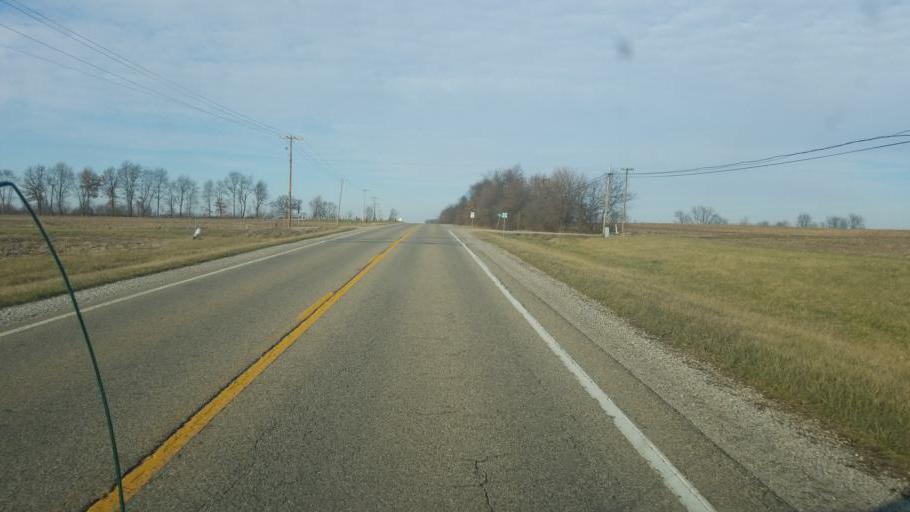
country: US
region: Illinois
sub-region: Lawrence County
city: Bridgeport
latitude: 38.6266
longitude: -87.6939
